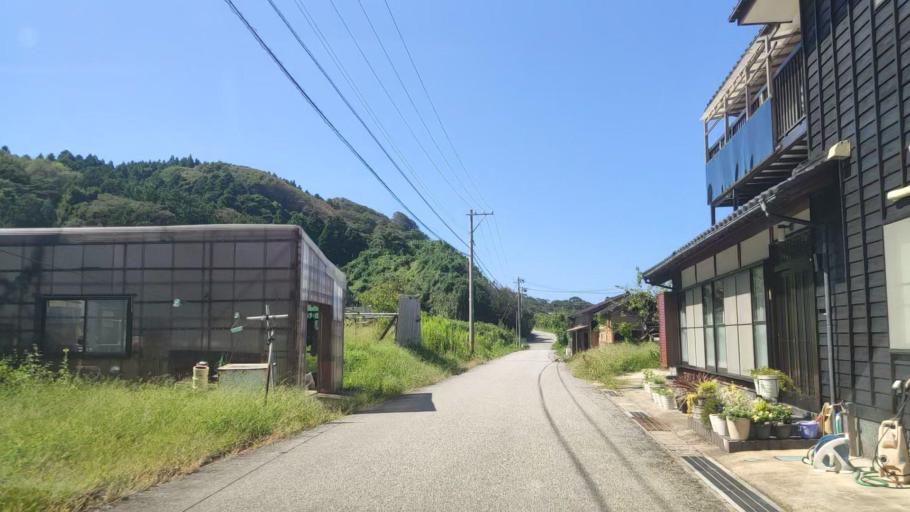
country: JP
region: Ishikawa
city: Nanao
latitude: 37.4480
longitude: 137.0559
